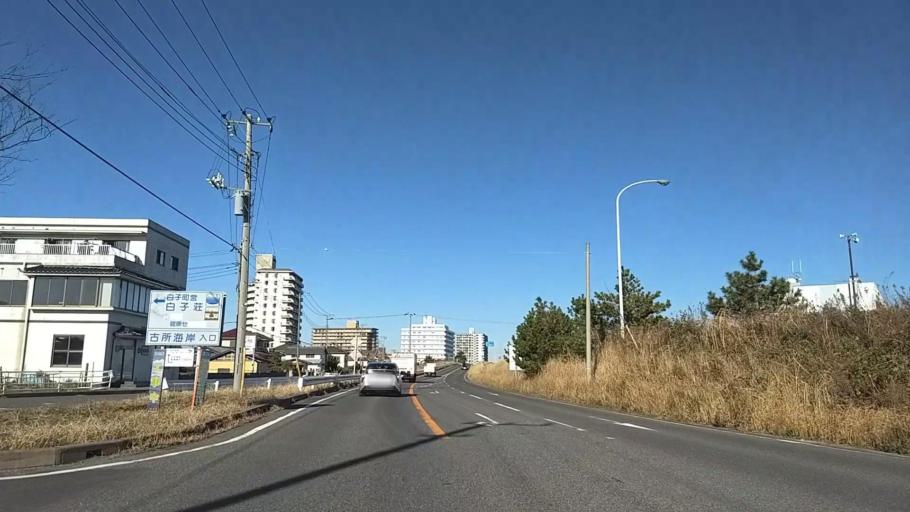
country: JP
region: Chiba
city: Mobara
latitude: 35.4465
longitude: 140.4013
